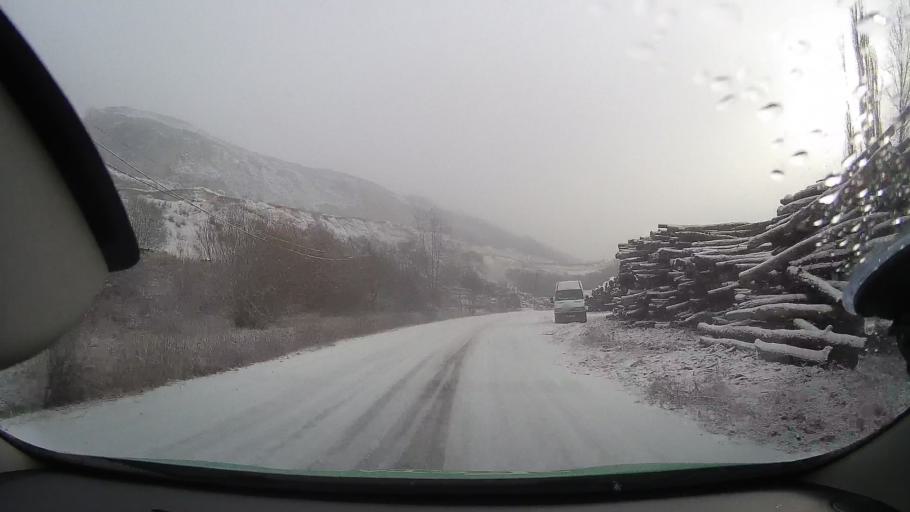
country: RO
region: Alba
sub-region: Comuna Livezile
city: Livezile
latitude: 46.3616
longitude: 23.6105
